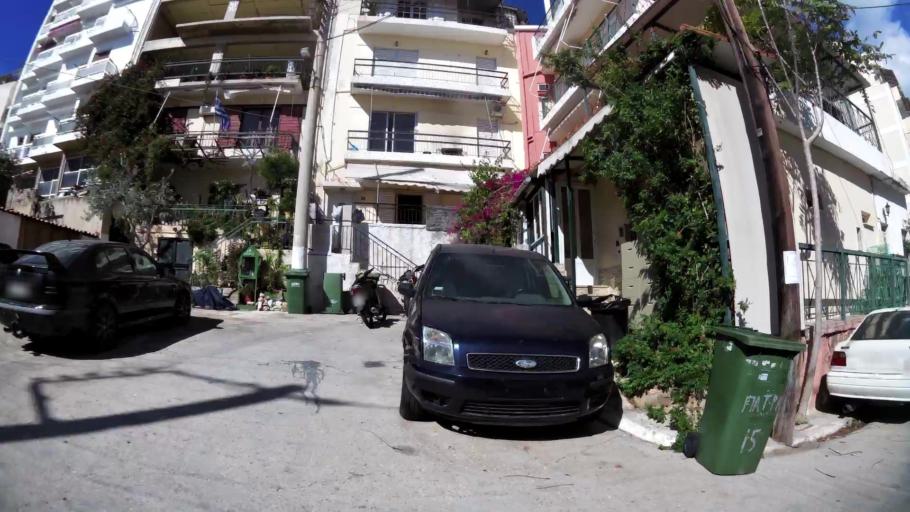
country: GR
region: Attica
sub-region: Nomos Piraios
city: Perama
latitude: 37.9689
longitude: 23.5638
